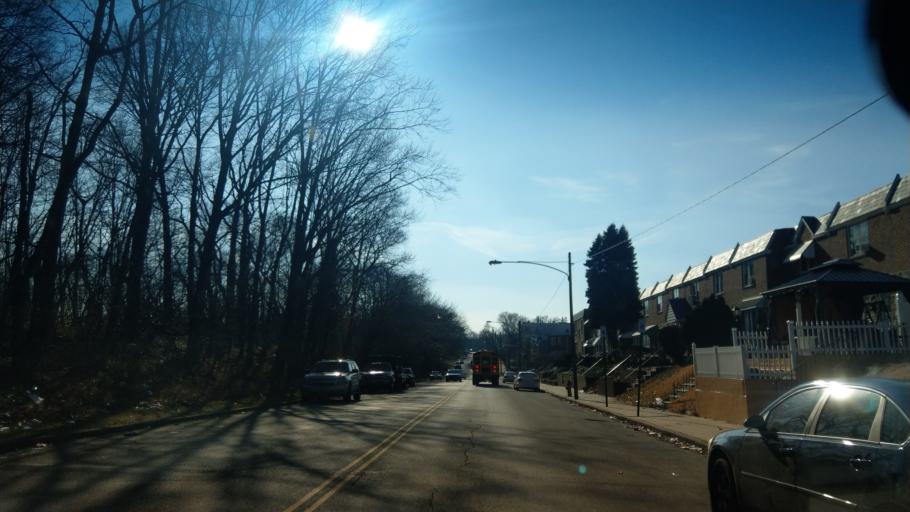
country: US
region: Pennsylvania
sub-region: Montgomery County
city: Rockledge
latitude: 40.0301
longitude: -75.1121
